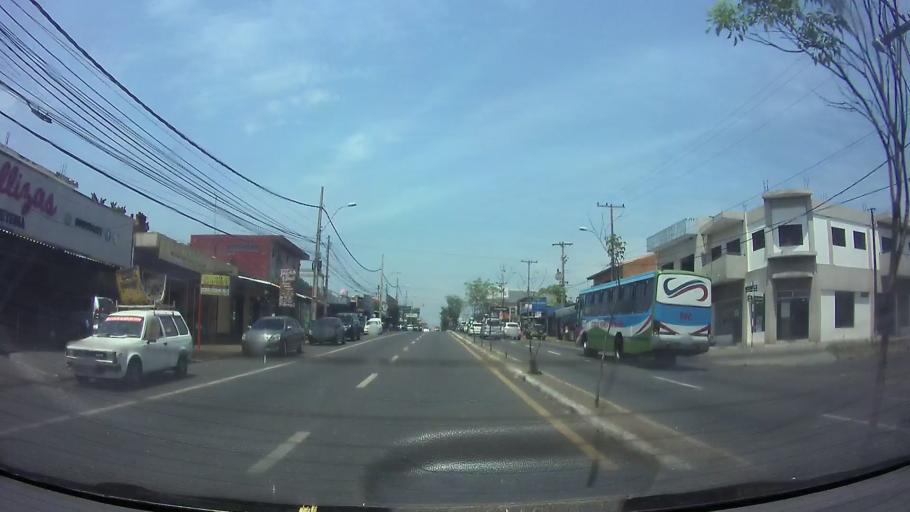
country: PY
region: Central
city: Itaugua
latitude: -25.3909
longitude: -57.3574
